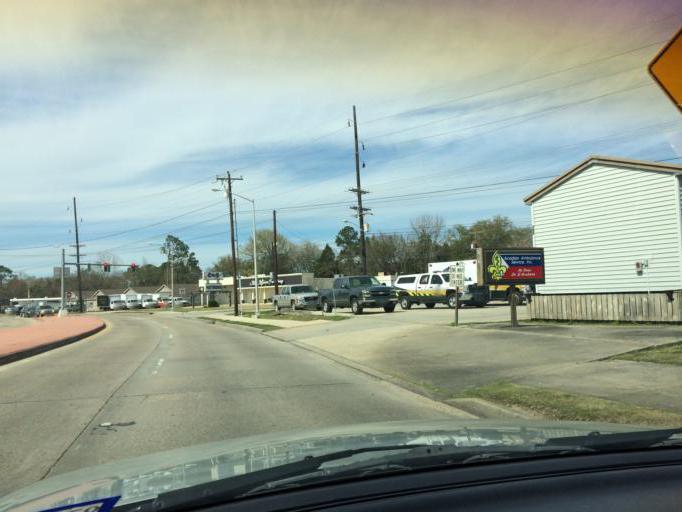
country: US
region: Louisiana
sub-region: Lafayette Parish
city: Lafayette
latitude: 30.1941
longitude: -92.0590
